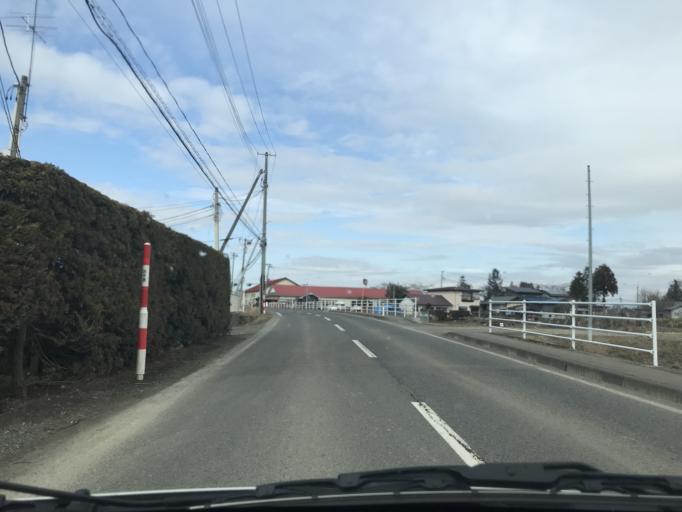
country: JP
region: Iwate
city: Hanamaki
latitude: 39.3480
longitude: 141.0477
